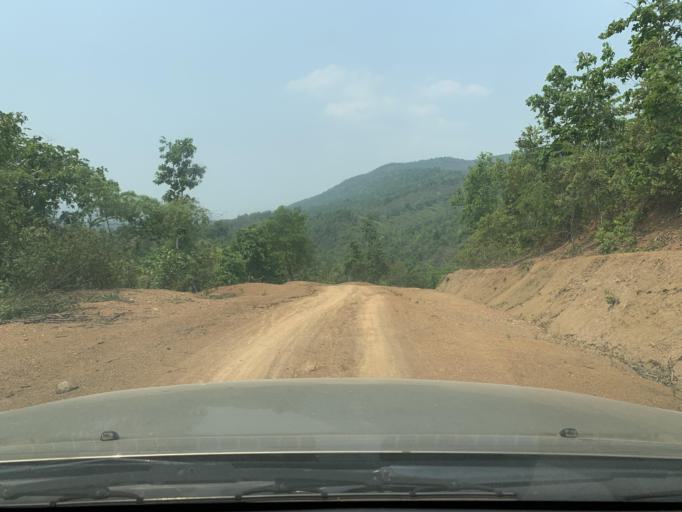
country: LA
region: Louangphabang
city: Louangphabang
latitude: 19.9377
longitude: 102.1337
